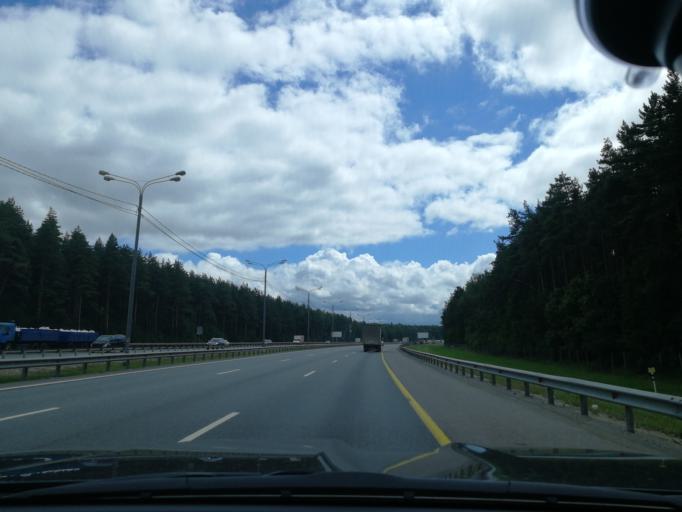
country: RU
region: Moskovskaya
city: Vostryakovo
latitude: 55.4418
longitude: 37.7981
